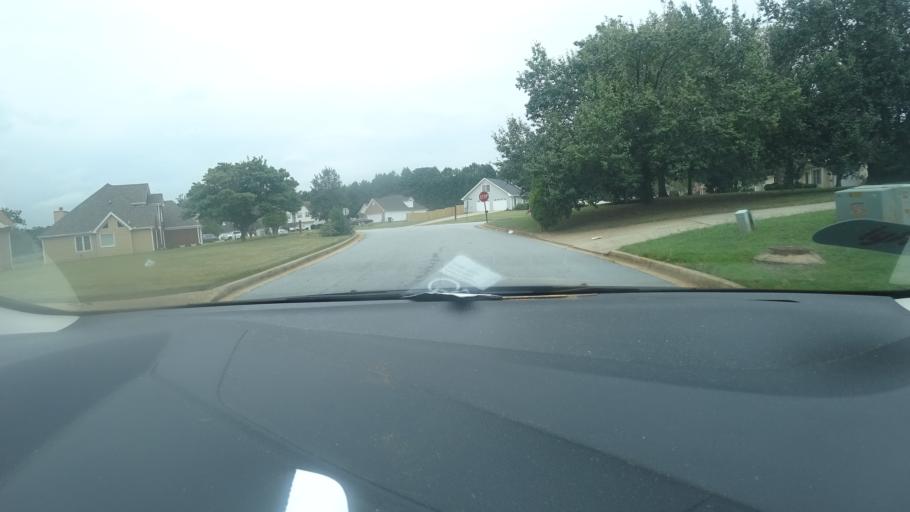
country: US
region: Georgia
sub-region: Newton County
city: Porterdale
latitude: 33.6099
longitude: -83.9410
